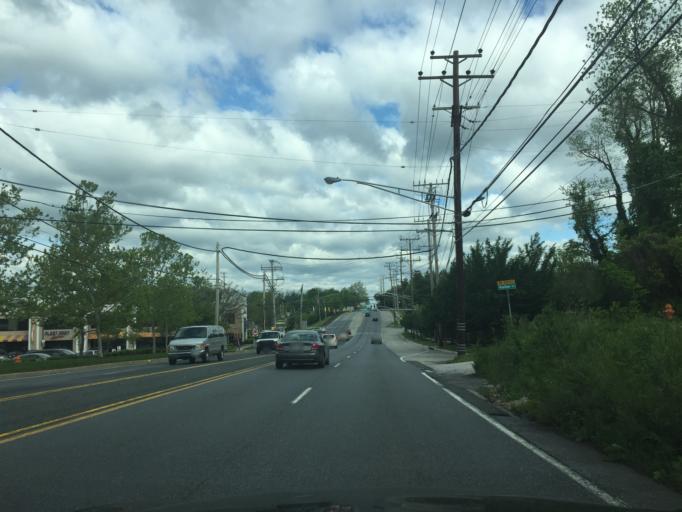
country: US
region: Maryland
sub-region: Baltimore County
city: Pikesville
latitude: 39.3898
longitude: -76.7399
